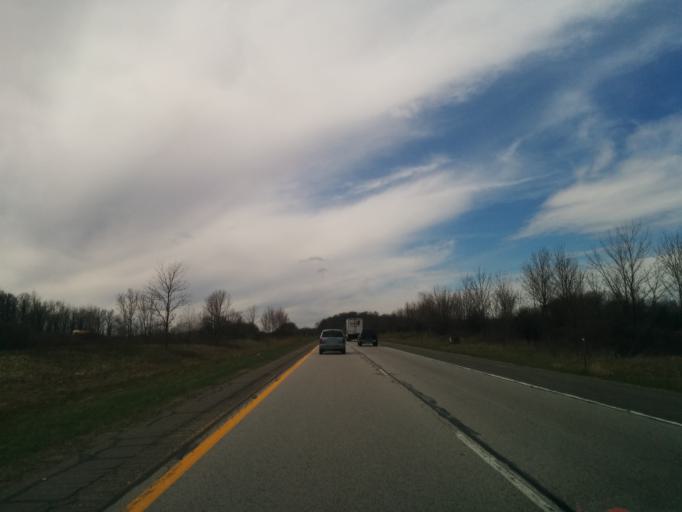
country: US
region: Michigan
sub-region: Ottawa County
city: Hudsonville
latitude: 42.8358
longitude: -85.9025
